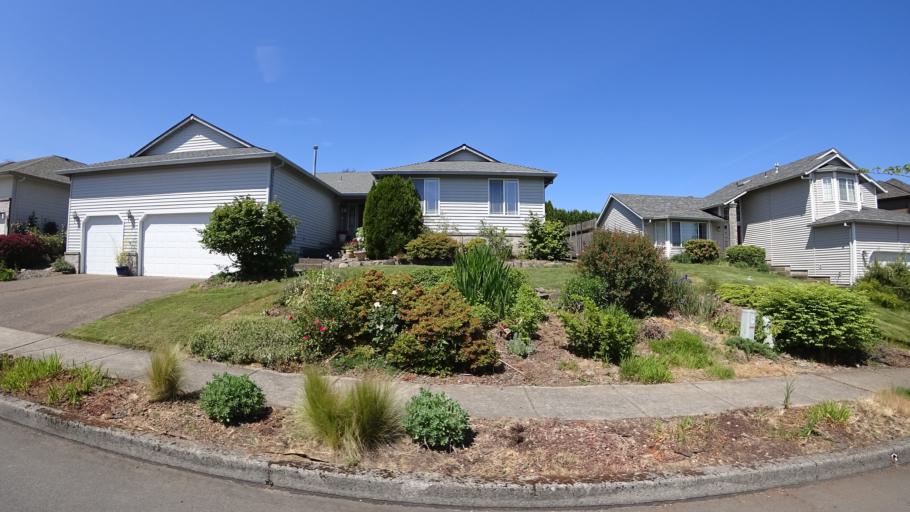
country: US
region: Oregon
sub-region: Multnomah County
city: Gresham
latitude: 45.4765
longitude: -122.4736
